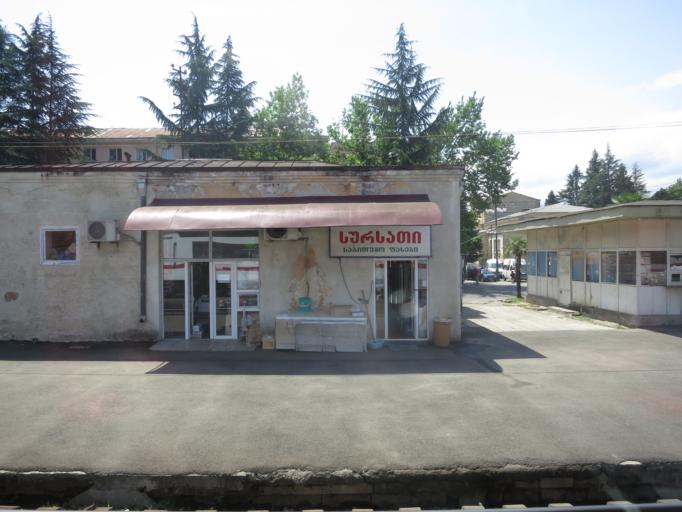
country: GE
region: Imereti
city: Zestap'oni
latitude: 42.1079
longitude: 43.0398
